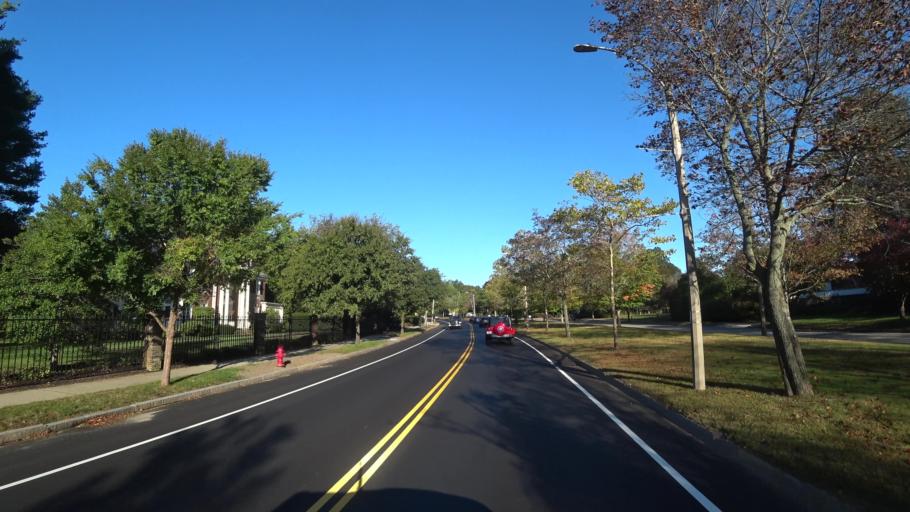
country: US
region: Massachusetts
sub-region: Middlesex County
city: Newton
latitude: 42.3371
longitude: -71.1968
